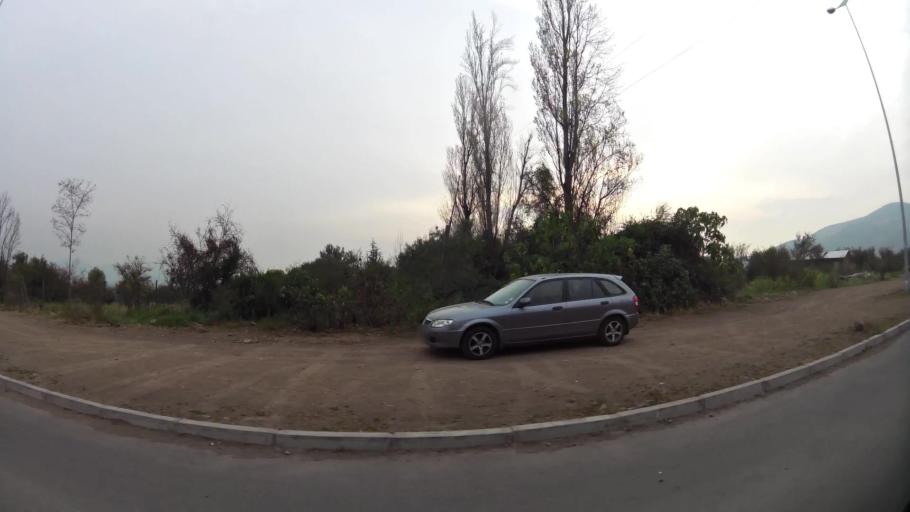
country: CL
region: Santiago Metropolitan
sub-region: Provincia de Chacabuco
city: Chicureo Abajo
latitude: -33.2613
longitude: -70.6186
